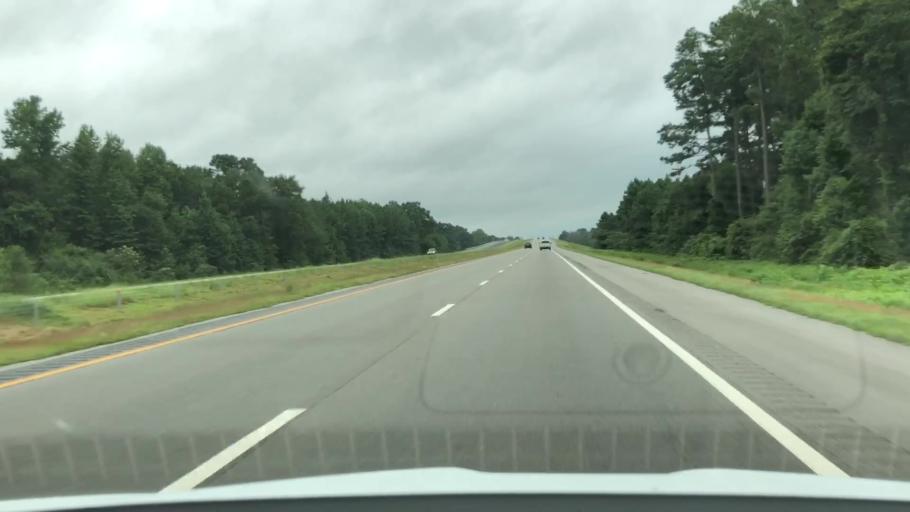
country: US
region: North Carolina
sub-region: Lenoir County
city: La Grange
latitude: 35.3362
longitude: -77.8437
